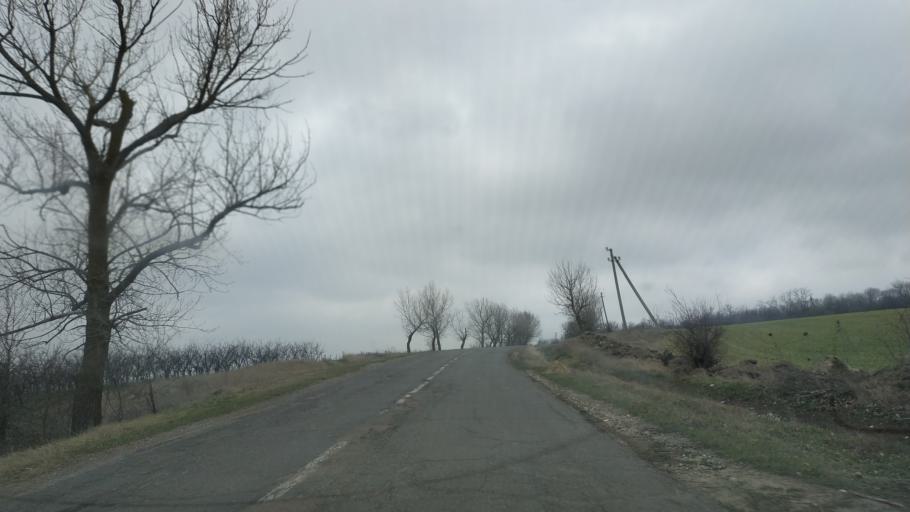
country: MD
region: Gagauzia
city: Bugeac
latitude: 46.3525
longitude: 28.7906
